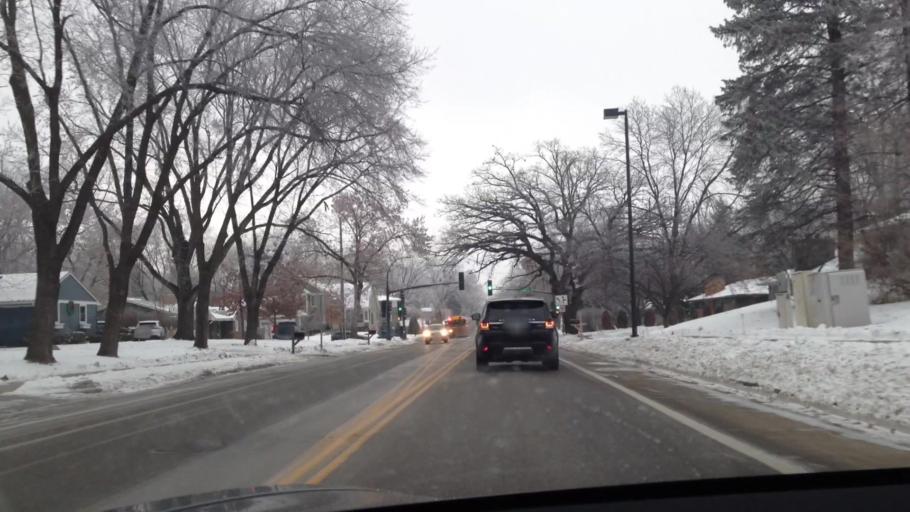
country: US
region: Minnesota
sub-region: Hennepin County
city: Edina
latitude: 44.8764
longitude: -93.3446
